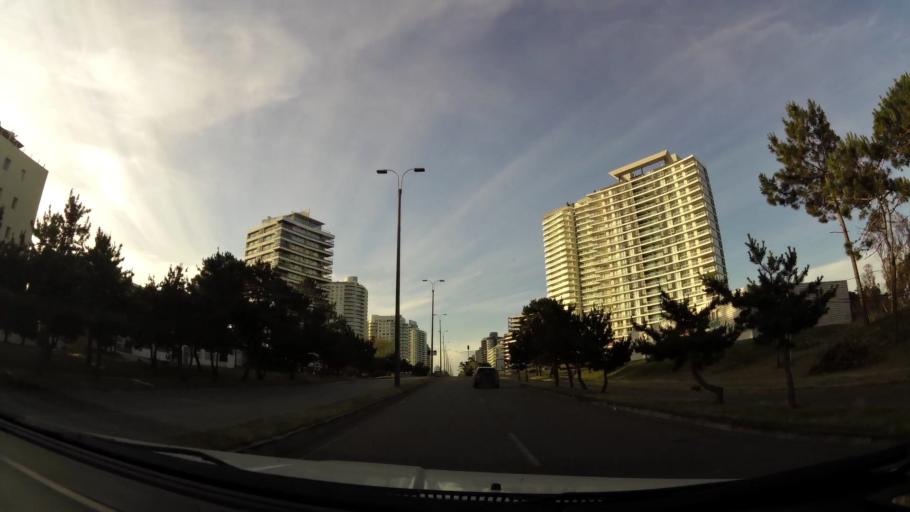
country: UY
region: Maldonado
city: Punta del Este
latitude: -34.9464
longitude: -54.9267
